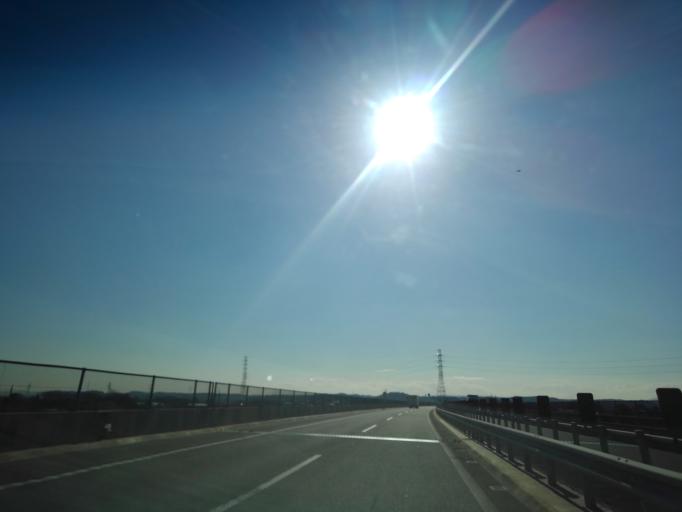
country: JP
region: Chiba
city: Kisarazu
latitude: 35.4043
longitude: 139.9653
